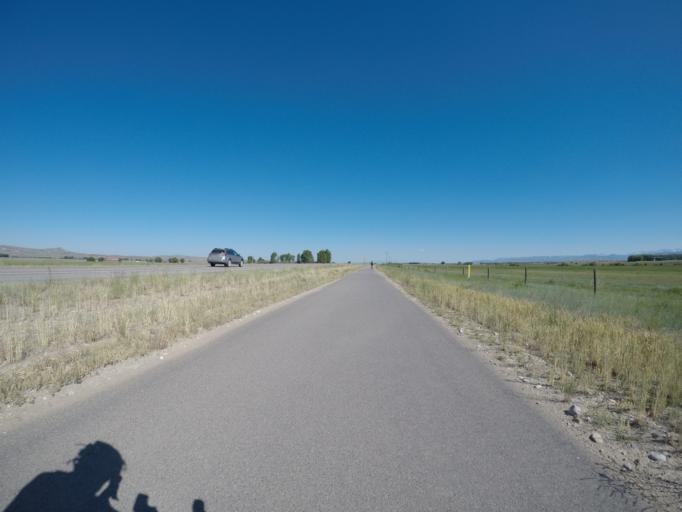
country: US
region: Wyoming
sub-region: Sublette County
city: Pinedale
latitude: 42.8210
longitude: -109.8408
